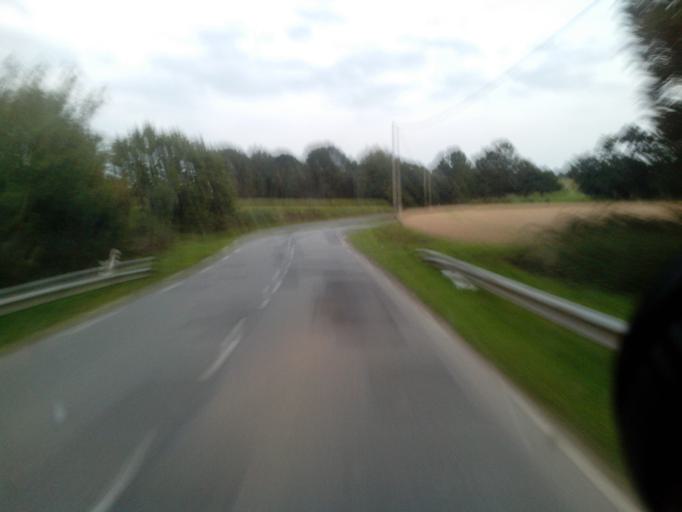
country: FR
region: Brittany
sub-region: Departement d'Ille-et-Vilaine
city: Iffendic
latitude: 48.1197
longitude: -2.0365
